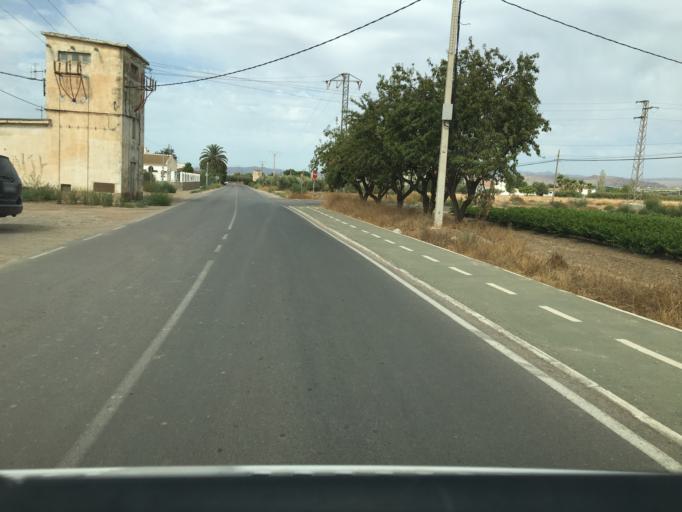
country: ES
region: Andalusia
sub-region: Provincia de Almeria
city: Huercal-Overa
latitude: 37.4224
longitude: -1.8866
